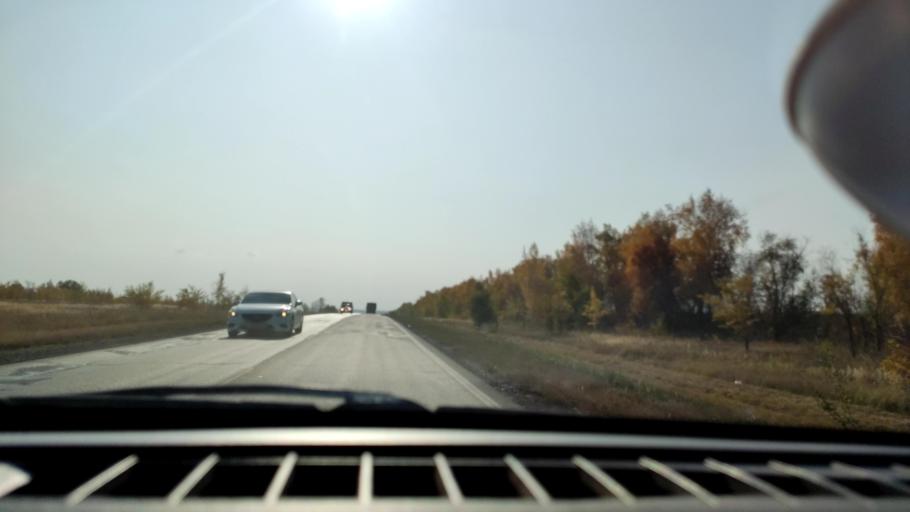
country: RU
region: Samara
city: Smyshlyayevka
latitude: 53.1169
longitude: 50.3623
